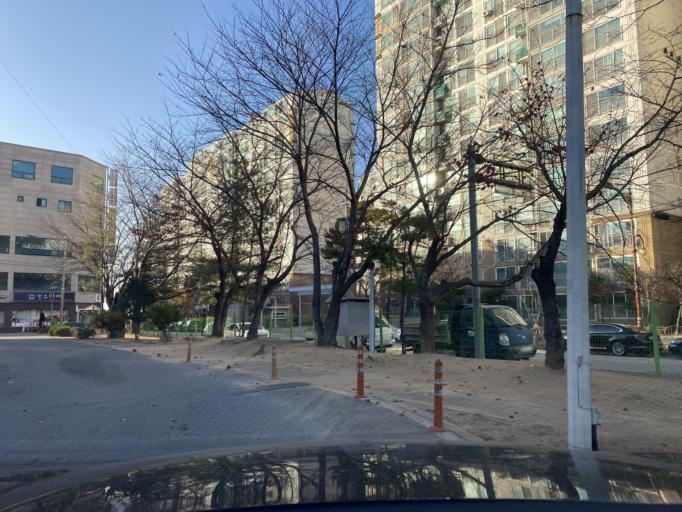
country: KR
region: Chungcheongnam-do
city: Yesan
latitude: 36.6948
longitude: 126.8328
